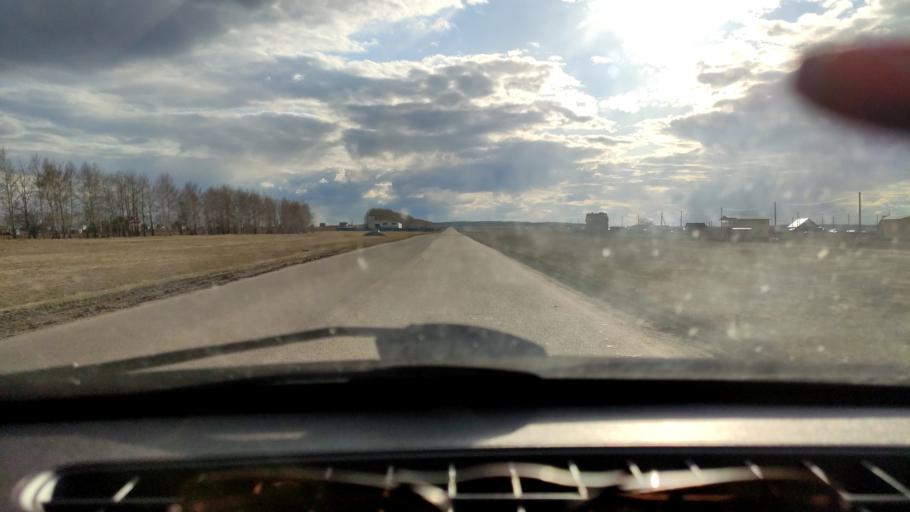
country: RU
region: Bashkortostan
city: Karmaskaly
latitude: 54.3532
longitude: 56.1381
